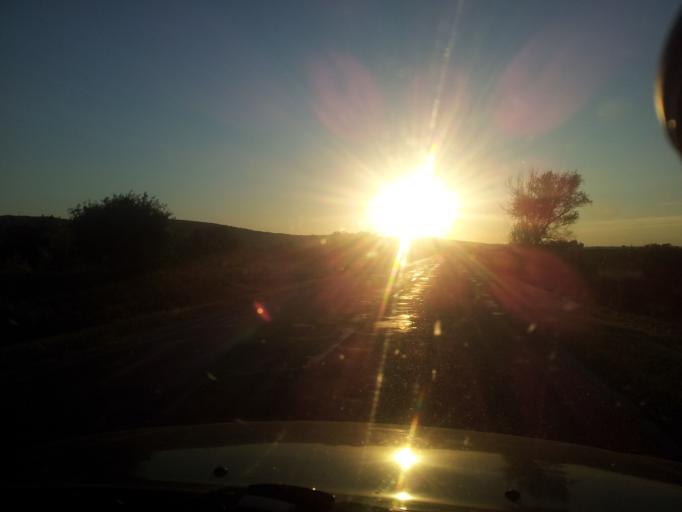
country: SK
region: Nitriansky
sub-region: Okres Nove Zamky
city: Sturovo
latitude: 47.8237
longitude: 18.6817
